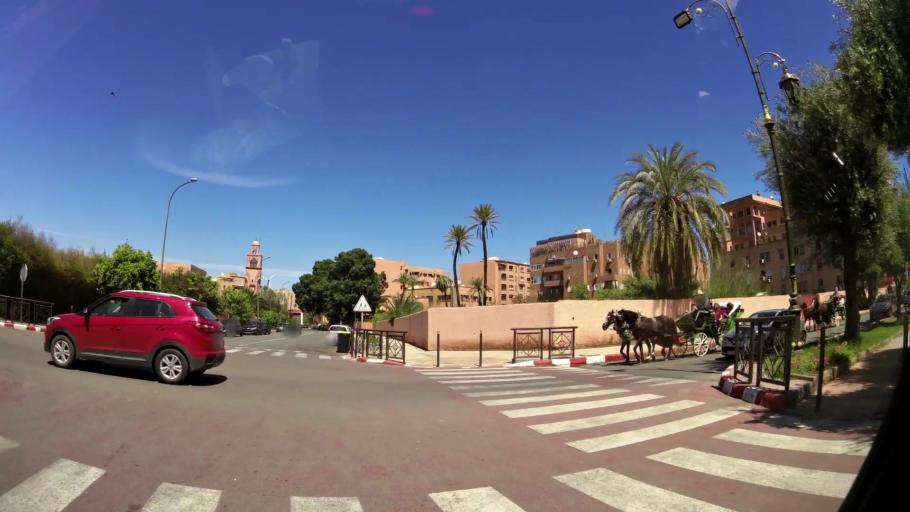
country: MA
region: Marrakech-Tensift-Al Haouz
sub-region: Marrakech
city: Marrakesh
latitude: 31.6286
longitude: -8.0048
